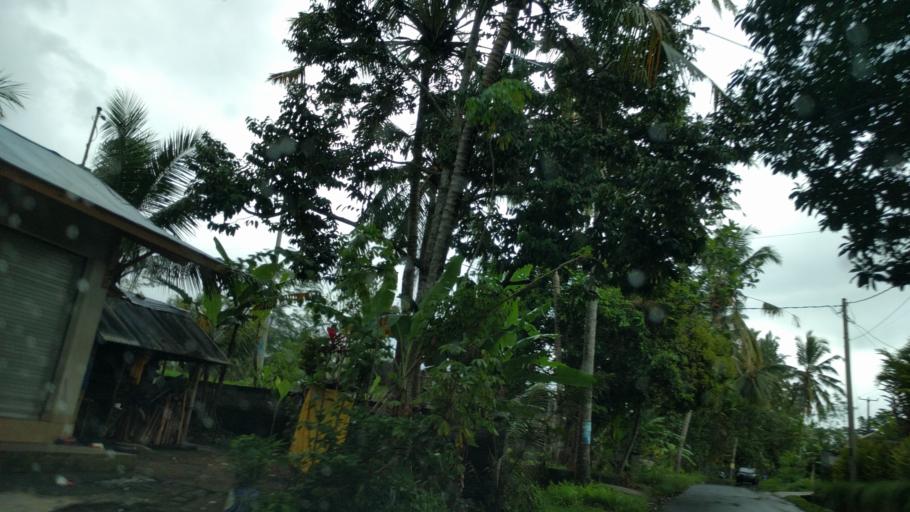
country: ID
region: Bali
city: Banjar Triwangsakeliki
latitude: -8.4610
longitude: 115.2593
